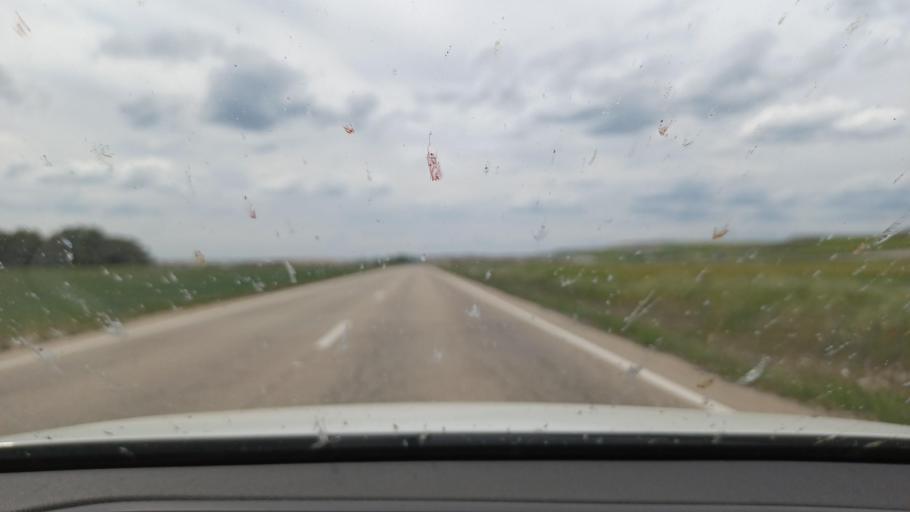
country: ES
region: Castille and Leon
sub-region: Provincia de Segovia
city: Frumales
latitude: 41.3831
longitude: -4.2290
